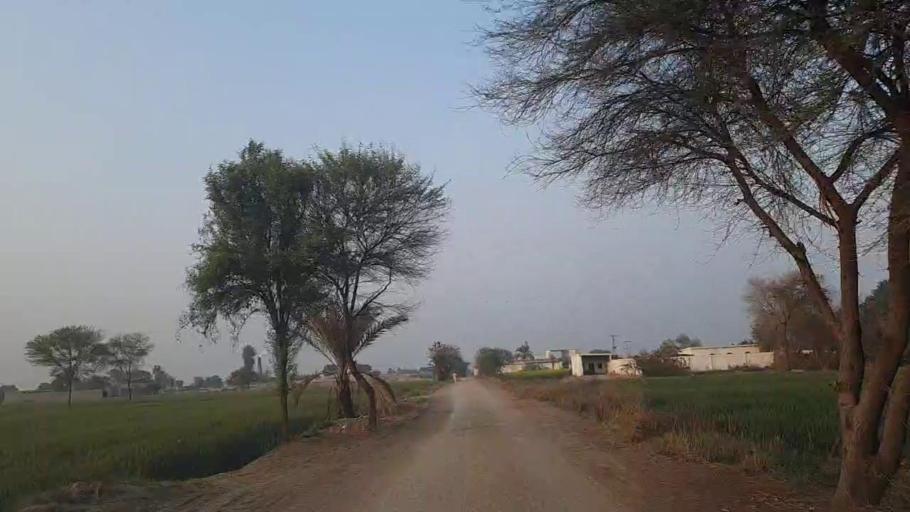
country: PK
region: Sindh
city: Nawabshah
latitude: 26.2792
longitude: 68.4648
